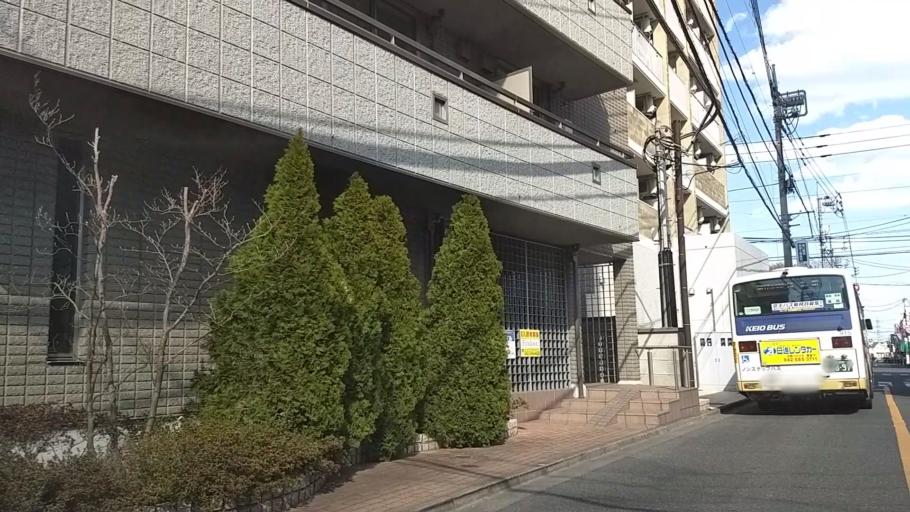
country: JP
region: Tokyo
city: Kokubunji
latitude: 35.6836
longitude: 139.4468
